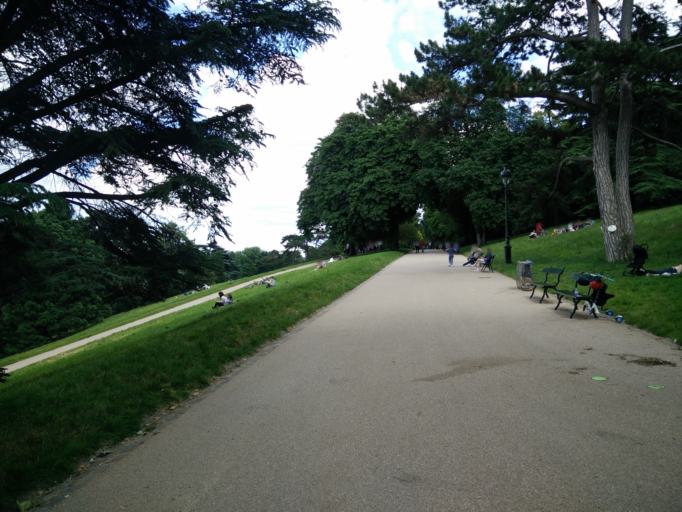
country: FR
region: Ile-de-France
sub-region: Departement de Seine-Saint-Denis
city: Le Pre-Saint-Gervais
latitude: 48.8794
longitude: 2.3806
